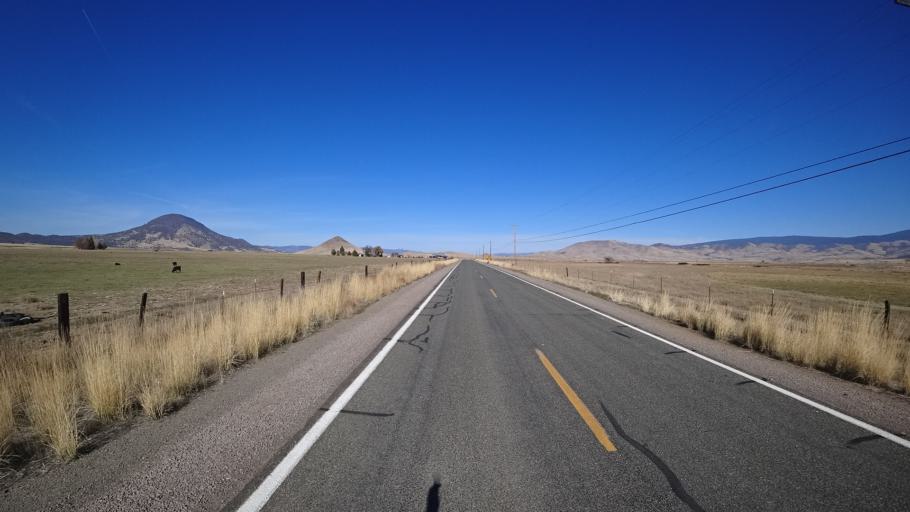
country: US
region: California
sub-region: Siskiyou County
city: Montague
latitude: 41.7903
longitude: -122.4716
